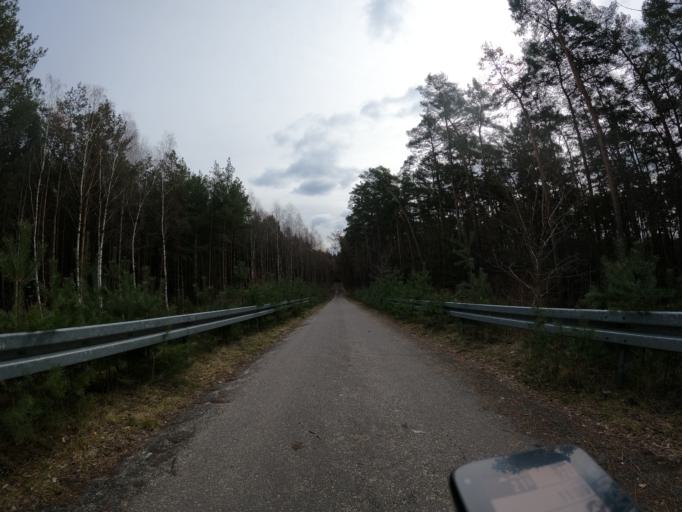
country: DE
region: Berlin
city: Bohnsdorf
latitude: 52.3933
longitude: 13.5979
